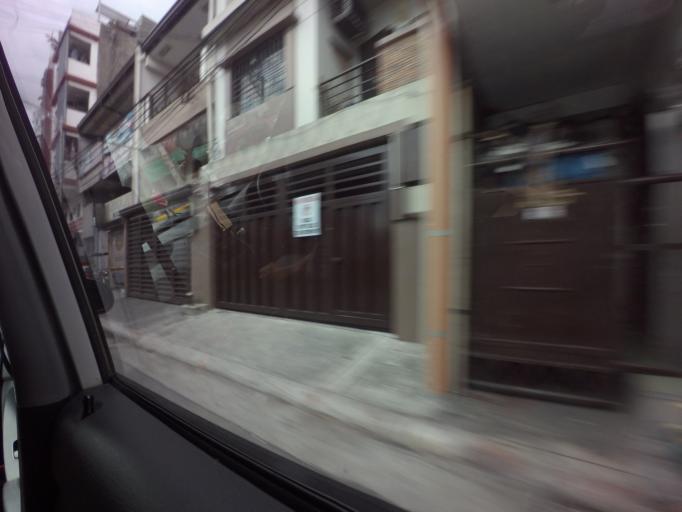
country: PH
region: Metro Manila
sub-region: City of Manila
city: Quiapo
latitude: 14.6061
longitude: 121.0076
